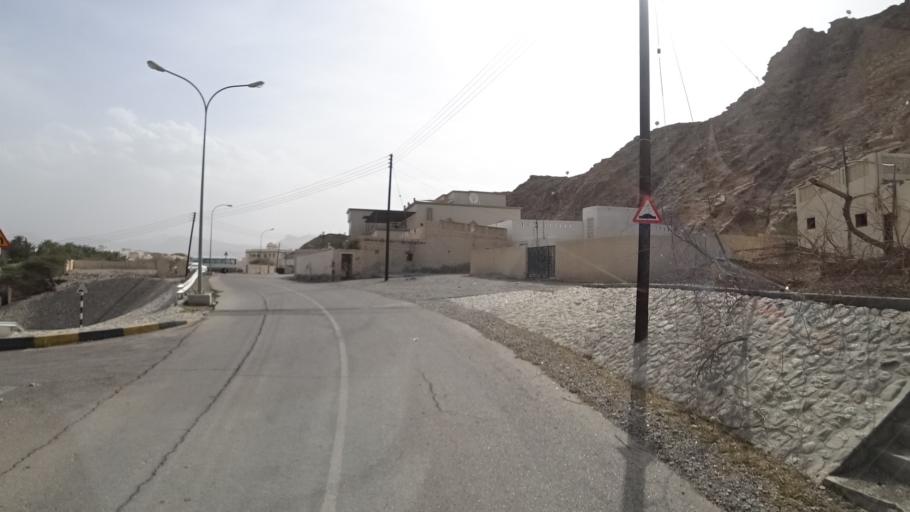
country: OM
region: Muhafazat Masqat
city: Bawshar
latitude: 23.3906
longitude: 58.5186
